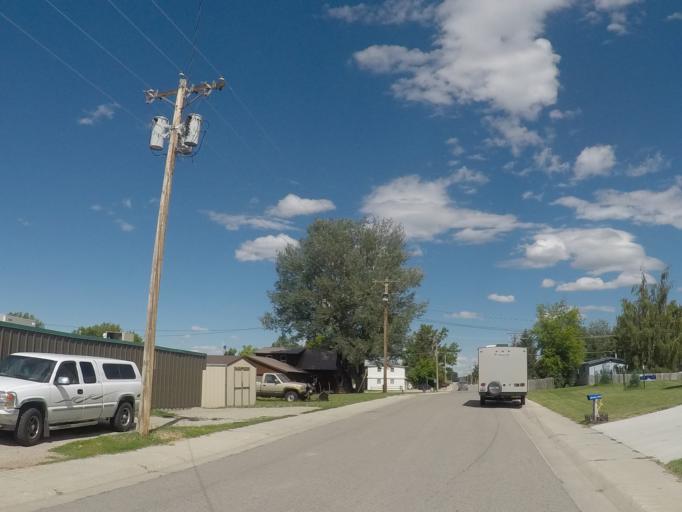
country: US
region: Wyoming
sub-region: Sheridan County
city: Sheridan
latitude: 44.8752
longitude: -107.2625
